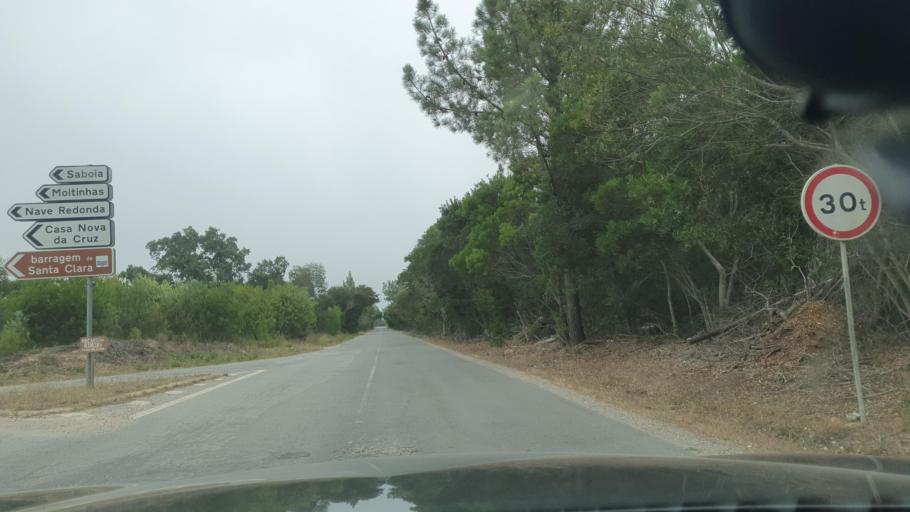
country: PT
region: Beja
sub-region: Odemira
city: Sao Teotonio
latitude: 37.5013
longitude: -8.6873
